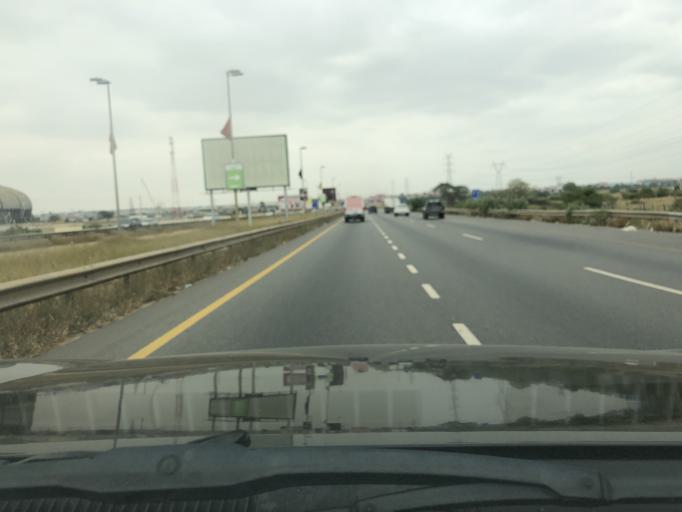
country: AO
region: Luanda
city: Luanda
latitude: -8.9741
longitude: 13.2805
